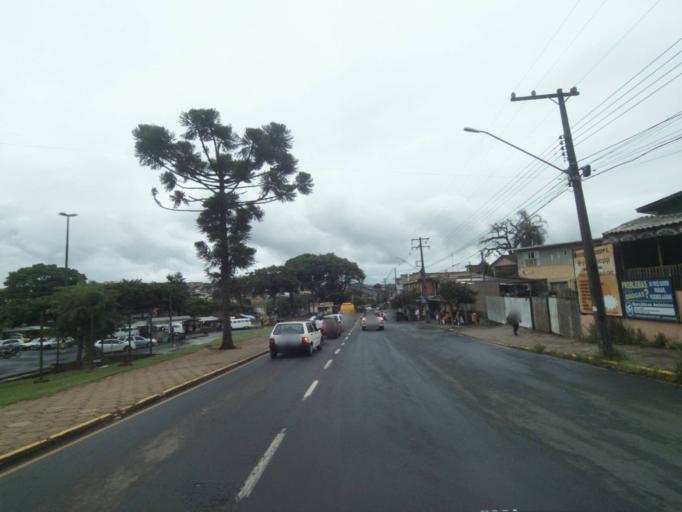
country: BR
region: Parana
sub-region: Telemaco Borba
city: Telemaco Borba
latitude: -24.3295
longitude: -50.6262
